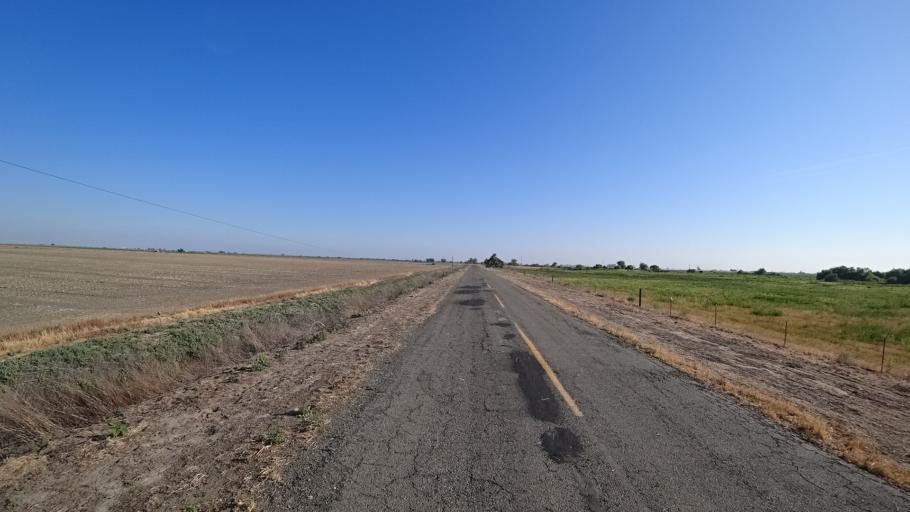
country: US
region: California
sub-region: Fresno County
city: Riverdale
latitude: 36.3969
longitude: -119.9278
